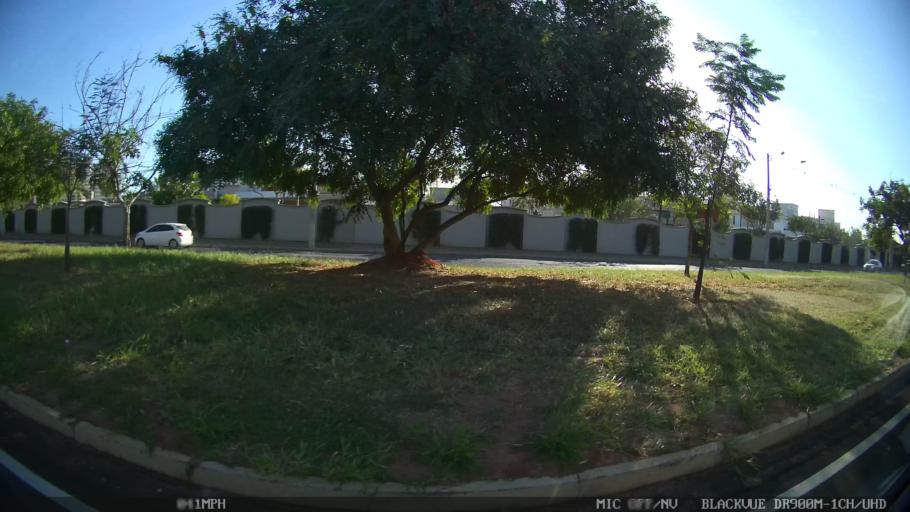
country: BR
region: Sao Paulo
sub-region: Sao Jose Do Rio Preto
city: Sao Jose do Rio Preto
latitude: -20.8613
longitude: -49.4119
